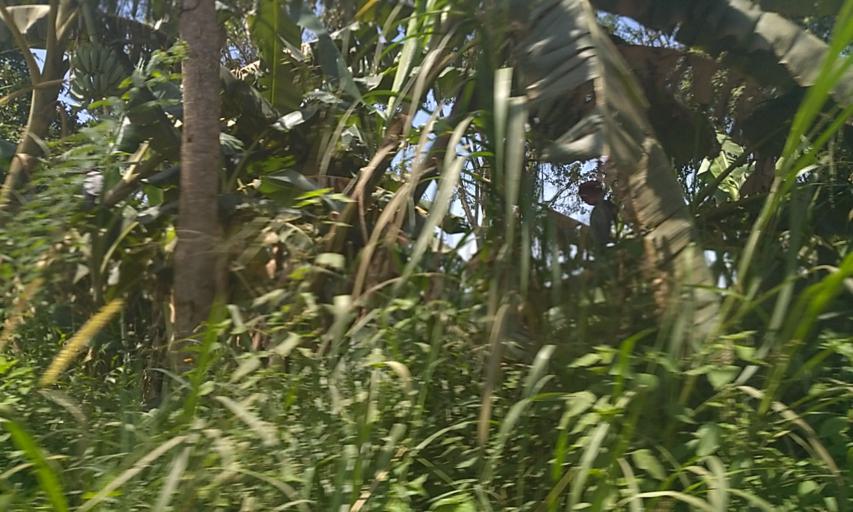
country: UG
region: Central Region
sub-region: Wakiso District
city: Wakiso
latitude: 0.4118
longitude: 32.4748
